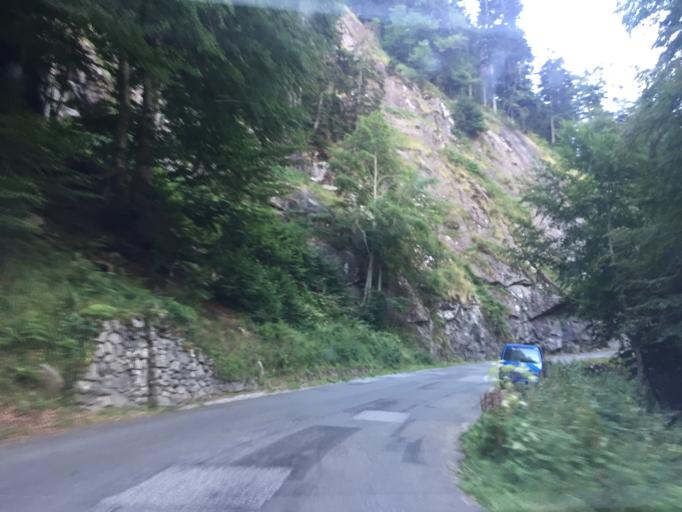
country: FR
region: Midi-Pyrenees
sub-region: Departement des Hautes-Pyrenees
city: Cauterets
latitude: 42.8677
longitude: -0.1136
